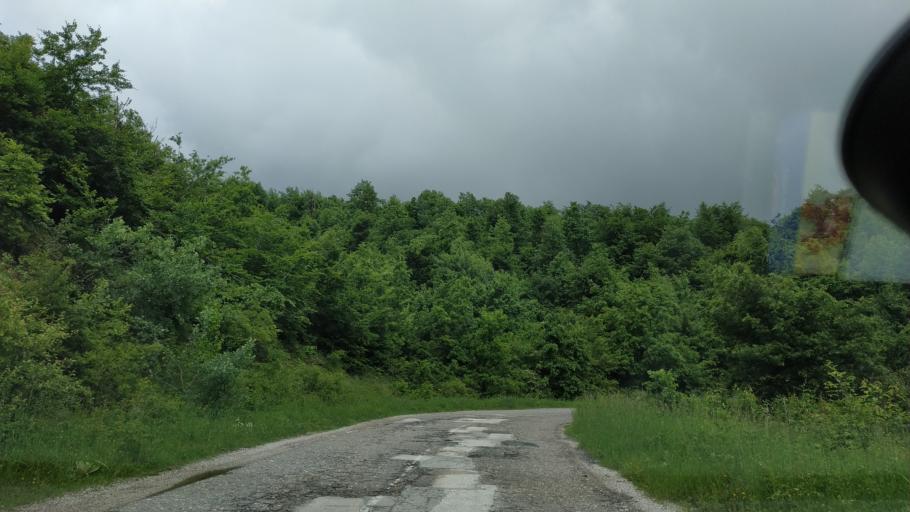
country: RS
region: Central Serbia
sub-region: Zajecarski Okrug
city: Soko Banja
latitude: 43.7183
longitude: 21.9446
